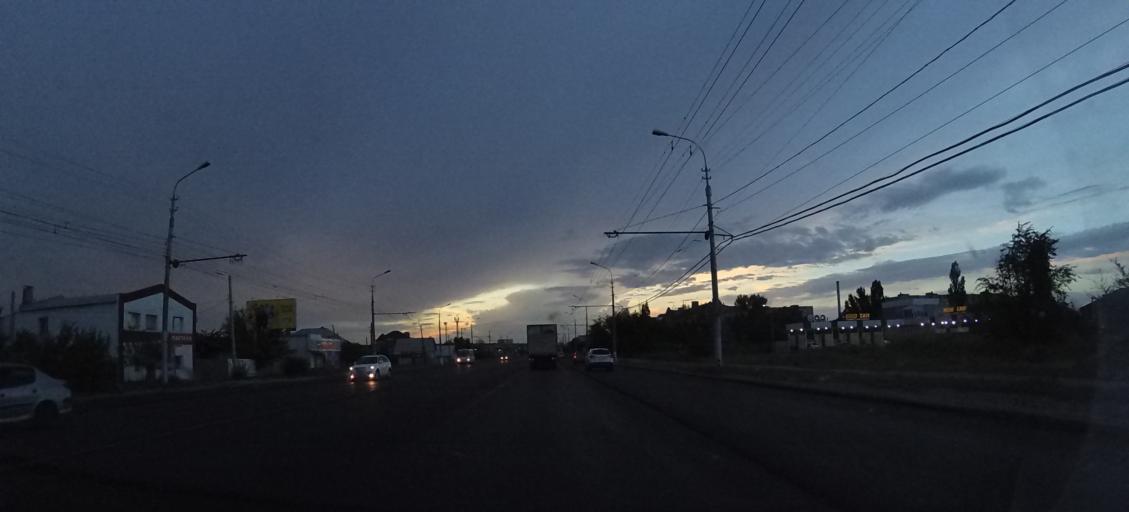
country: RU
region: Volgograd
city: Volgograd
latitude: 48.5858
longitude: 44.4218
